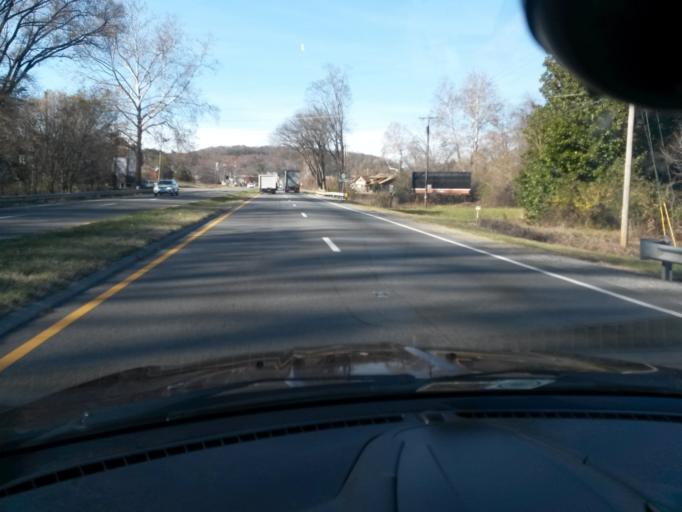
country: US
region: Virginia
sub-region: Roanoke County
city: Narrows
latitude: 37.2012
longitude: -79.9465
